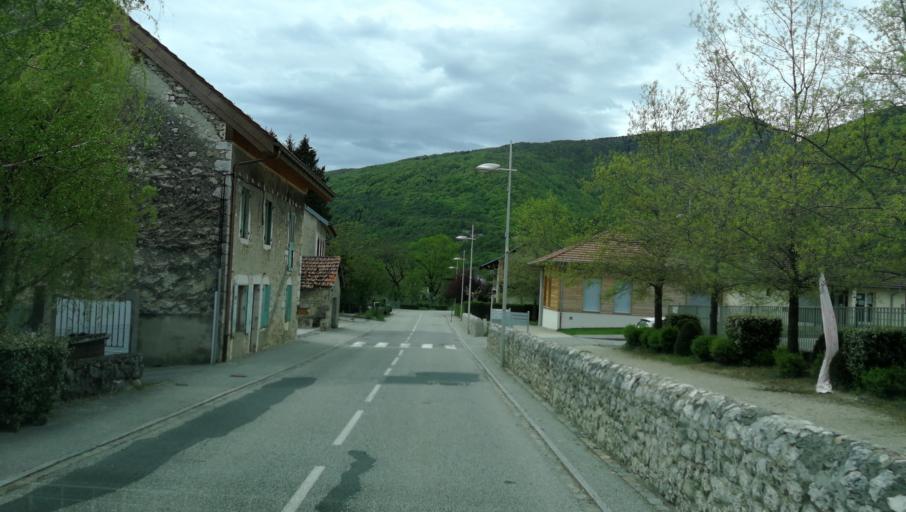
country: FR
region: Rhone-Alpes
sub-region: Departement de l'Ain
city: Bellegarde-sur-Valserine
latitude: 46.0048
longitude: 5.7848
